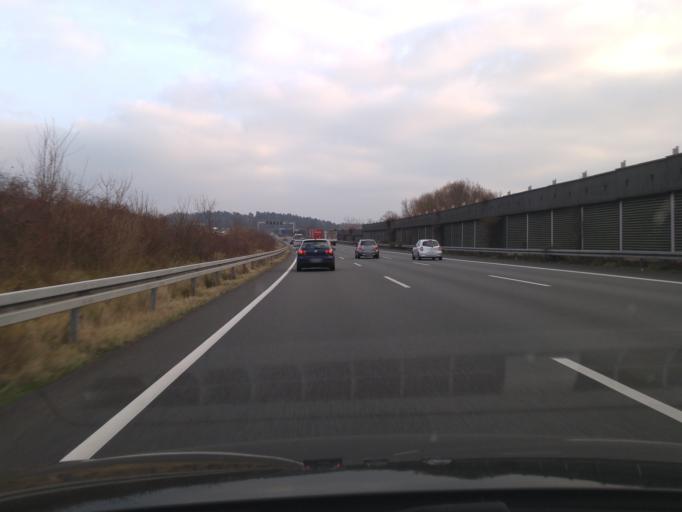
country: DE
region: Lower Saxony
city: Mariental
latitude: 52.2721
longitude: 10.9499
